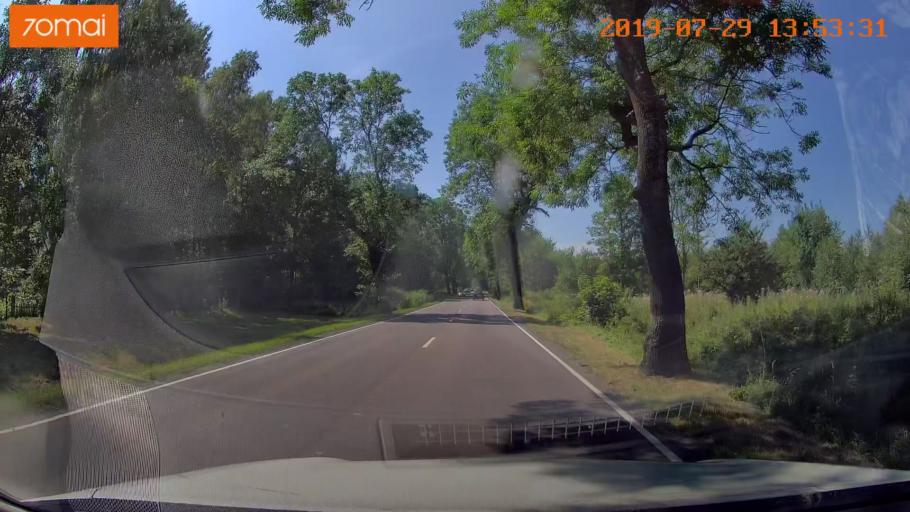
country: RU
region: Kaliningrad
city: Primorsk
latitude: 54.7289
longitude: 19.9789
